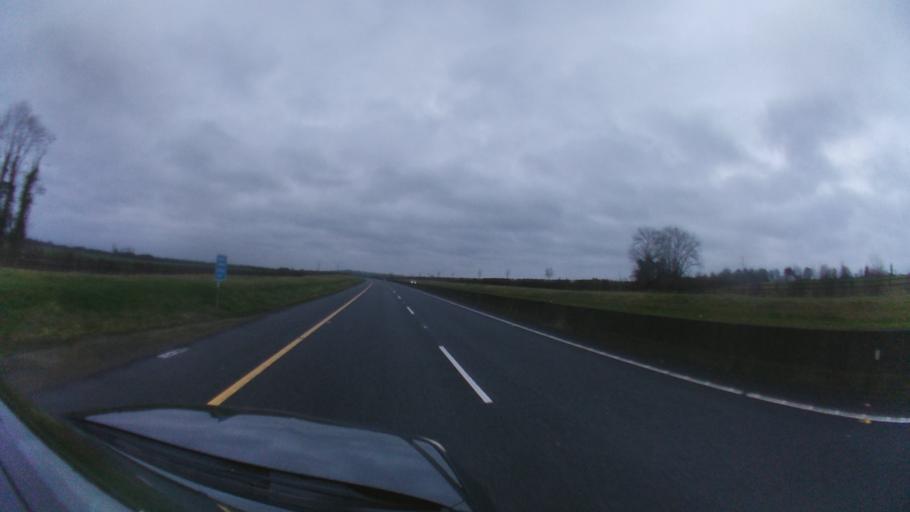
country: IE
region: Leinster
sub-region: Kildare
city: Moone
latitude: 52.9667
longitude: -6.8562
